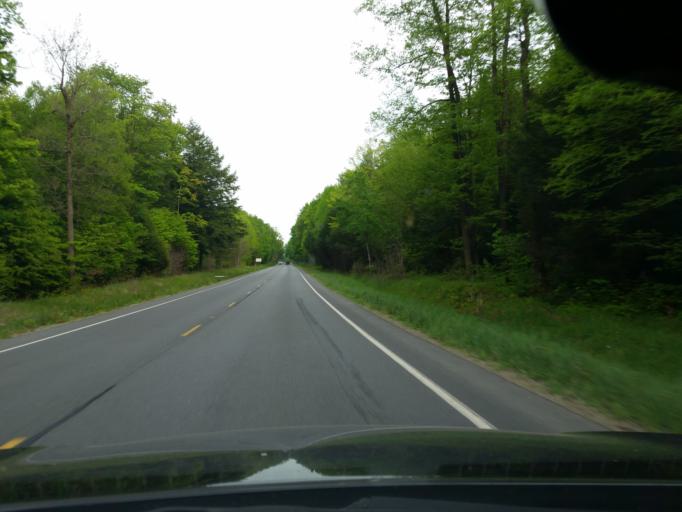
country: US
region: Pennsylvania
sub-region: McKean County
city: Kane
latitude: 41.5766
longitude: -78.9230
